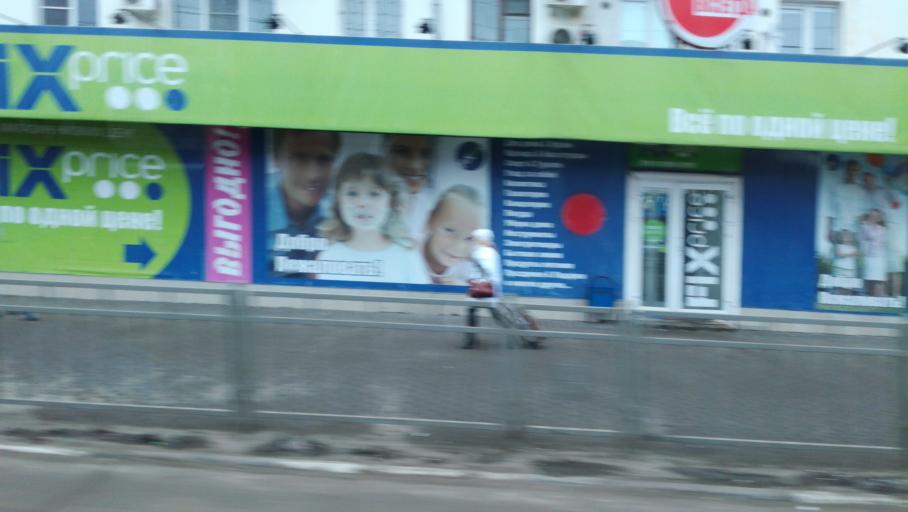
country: RU
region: Tula
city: Tula
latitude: 54.1989
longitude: 37.5821
